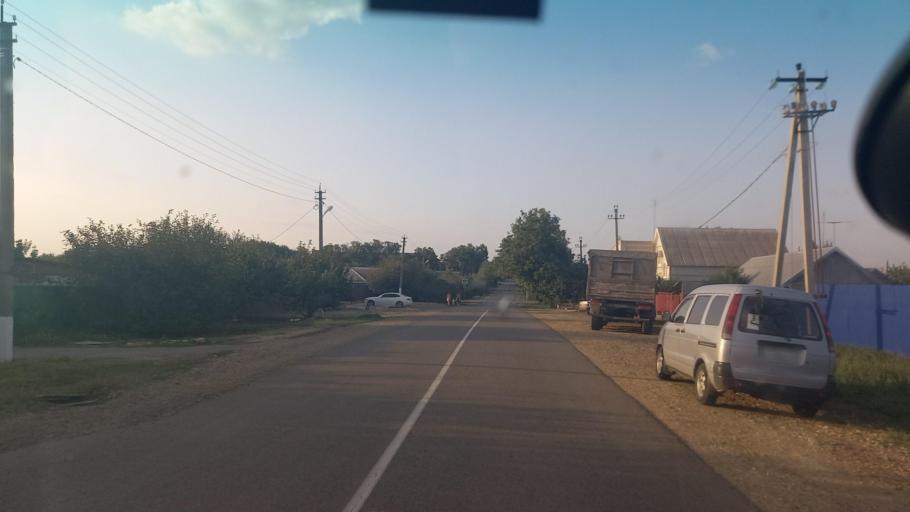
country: RU
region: Adygeya
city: Khatukay
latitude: 45.2949
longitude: 39.5573
